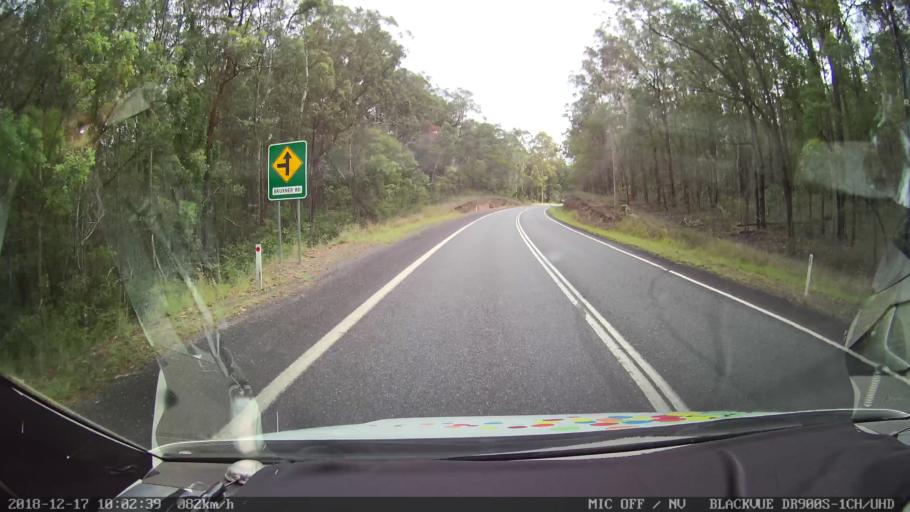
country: AU
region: New South Wales
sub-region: Tenterfield Municipality
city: Carrolls Creek
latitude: -28.9008
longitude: 152.4537
